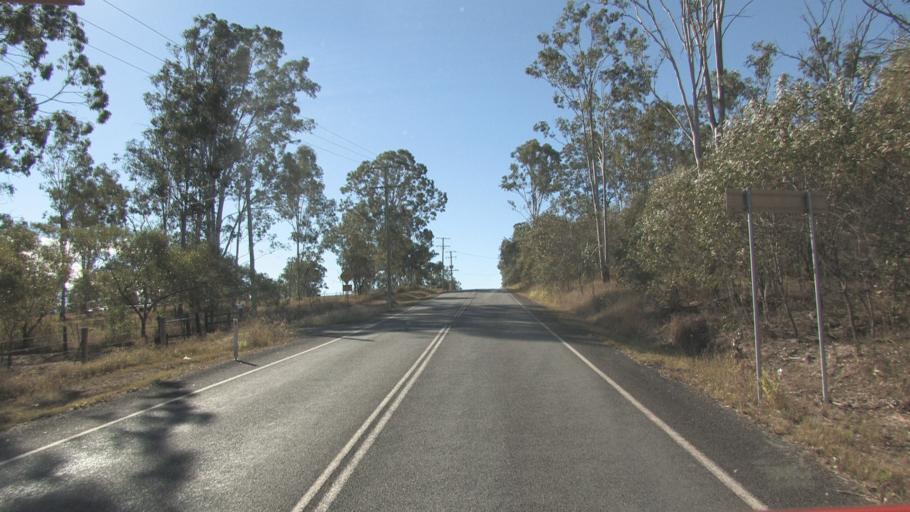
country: AU
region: Queensland
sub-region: Logan
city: Cedar Vale
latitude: -27.8323
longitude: 153.0527
